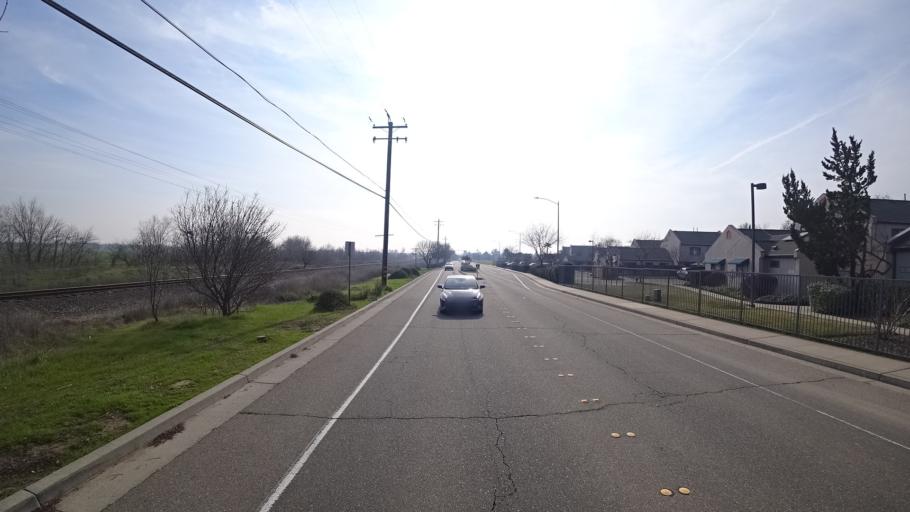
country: US
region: California
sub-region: Yolo County
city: Davis
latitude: 38.5750
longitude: -121.7477
